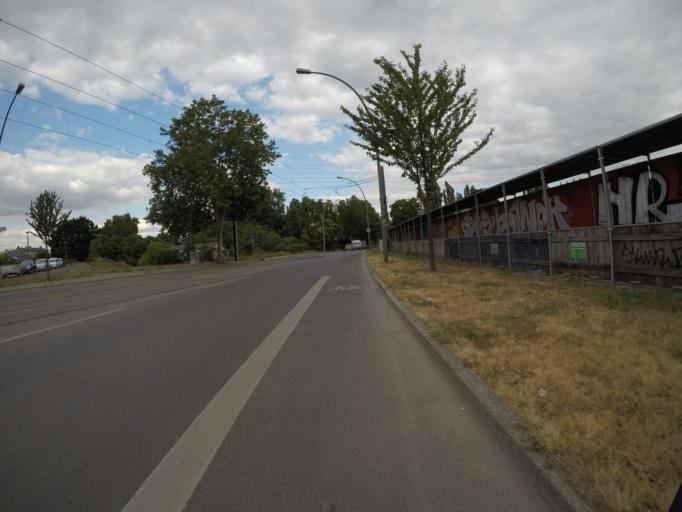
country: DE
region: Berlin
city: Karlshorst
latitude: 52.4841
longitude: 13.5112
